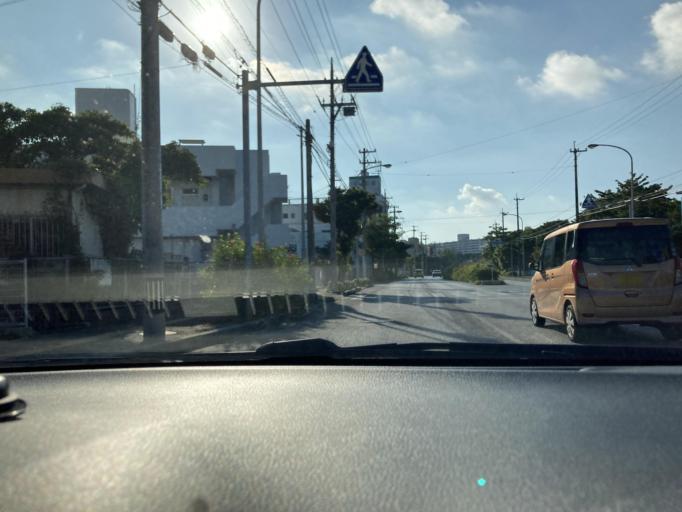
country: JP
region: Okinawa
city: Naha-shi
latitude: 26.2398
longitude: 127.6931
